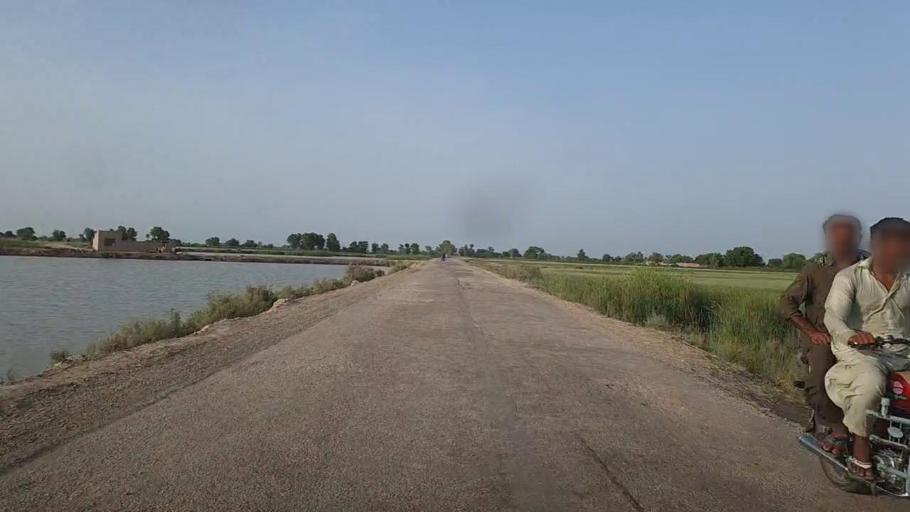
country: PK
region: Sindh
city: Ubauro
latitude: 28.0961
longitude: 69.8079
